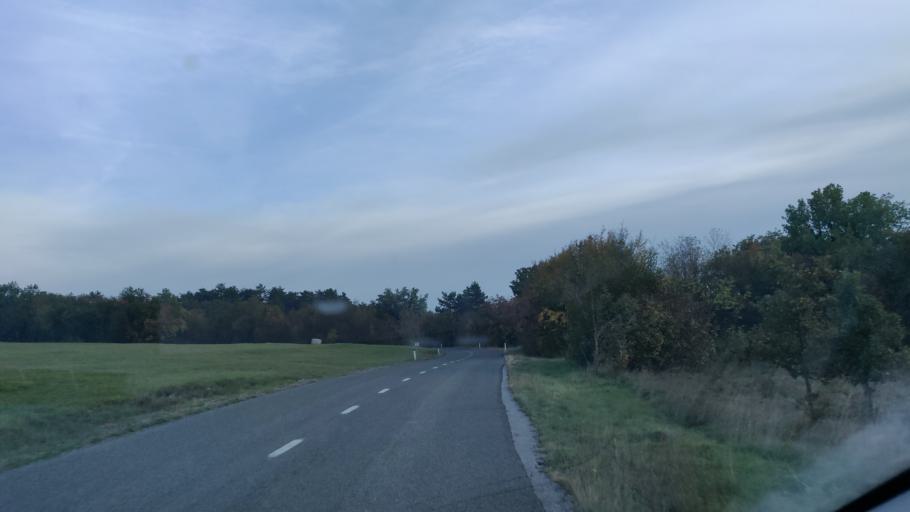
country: IT
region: Friuli Venezia Giulia
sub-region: Provincia di Trieste
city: Zolla
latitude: 45.8008
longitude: 13.8509
